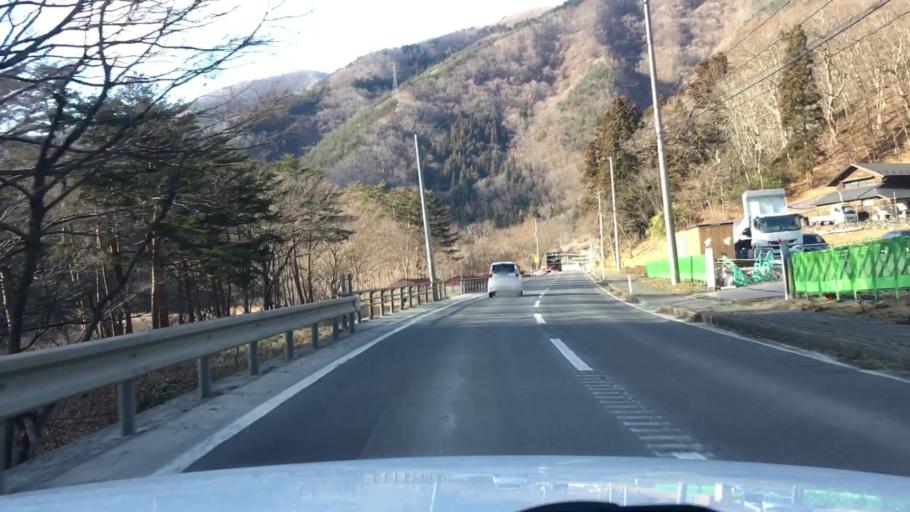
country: JP
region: Iwate
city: Miyako
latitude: 39.6018
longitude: 141.7020
